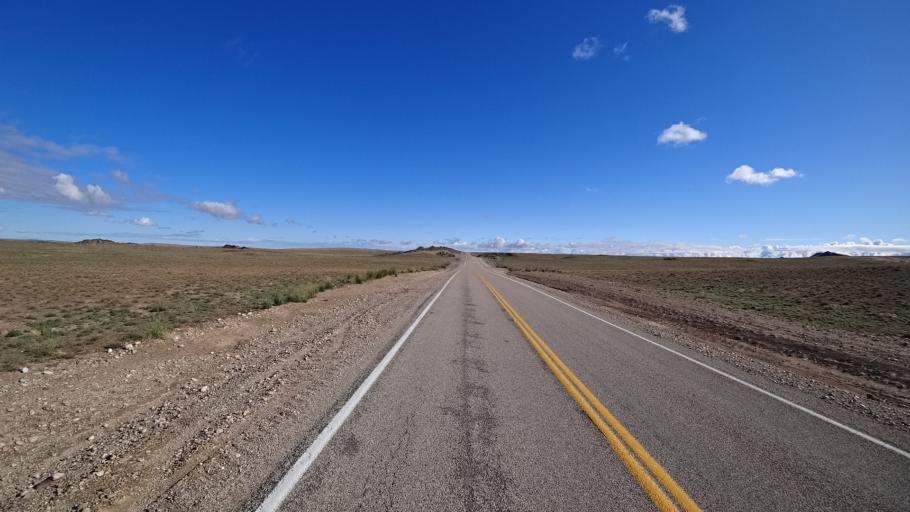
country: US
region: Idaho
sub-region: Ada County
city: Kuna
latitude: 43.3602
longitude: -116.4140
